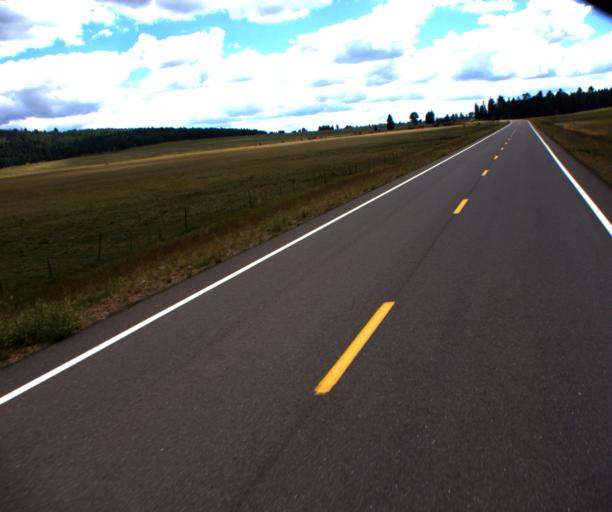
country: US
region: Arizona
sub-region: Apache County
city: Eagar
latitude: 33.9956
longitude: -109.5213
